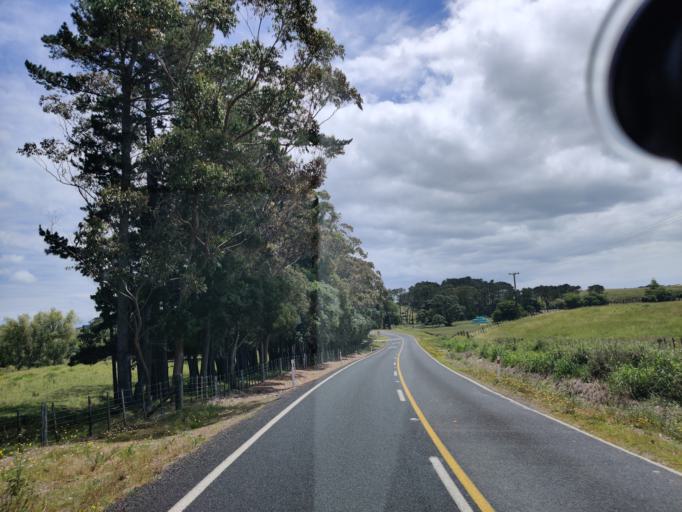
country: NZ
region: Northland
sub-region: Far North District
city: Kaitaia
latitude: -34.7104
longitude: 173.0350
